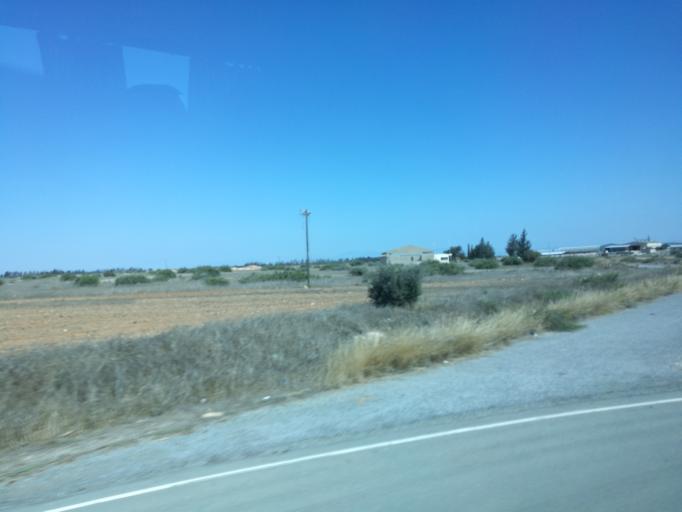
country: CY
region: Ammochostos
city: Achna
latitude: 35.0721
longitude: 33.8195
